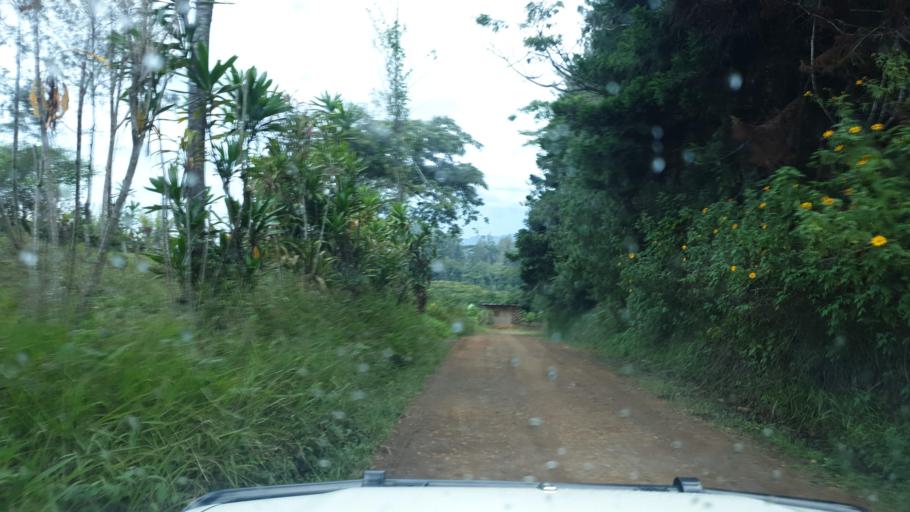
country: PG
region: Eastern Highlands
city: Goroka
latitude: -5.9646
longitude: 145.2748
